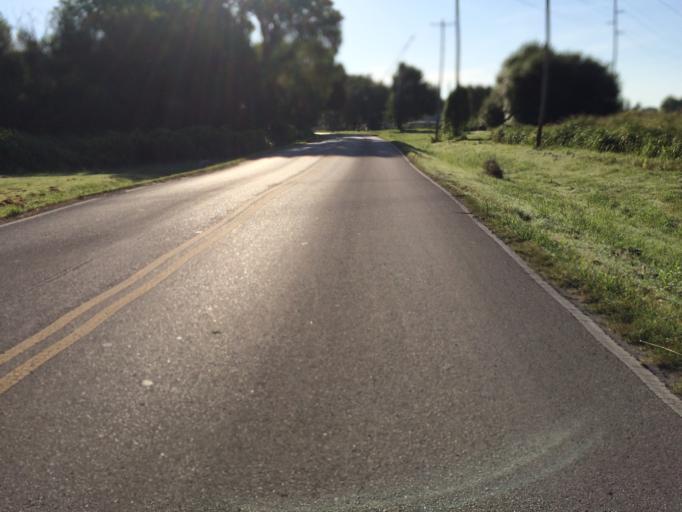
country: US
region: Oklahoma
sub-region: McClain County
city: Goldsby
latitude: 35.1736
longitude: -97.4467
